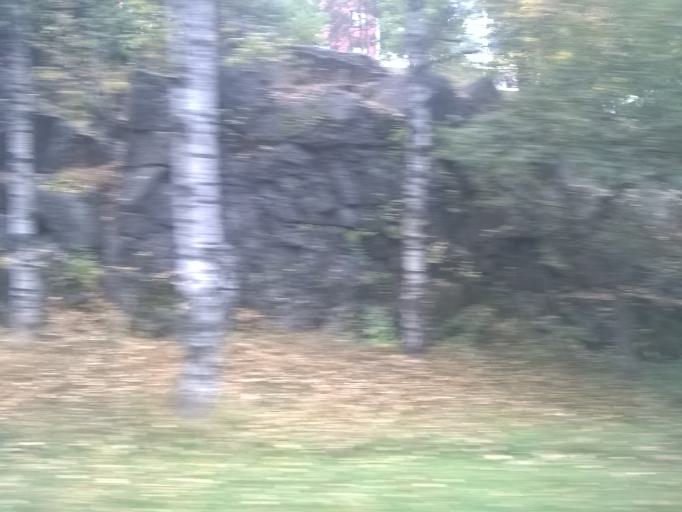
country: FI
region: Pirkanmaa
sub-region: Tampere
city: Tampere
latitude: 61.4458
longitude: 23.8366
